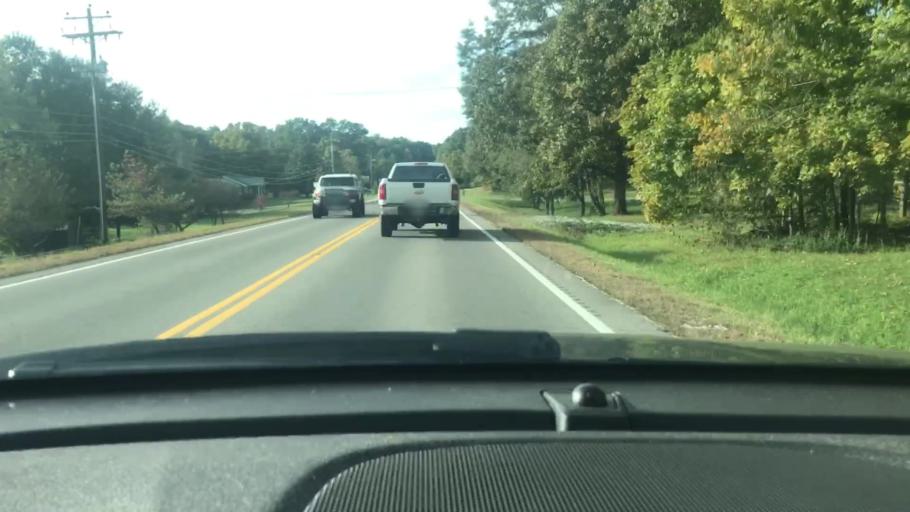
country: US
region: Tennessee
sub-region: Williamson County
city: Fairview
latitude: 35.9892
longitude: -87.1222
